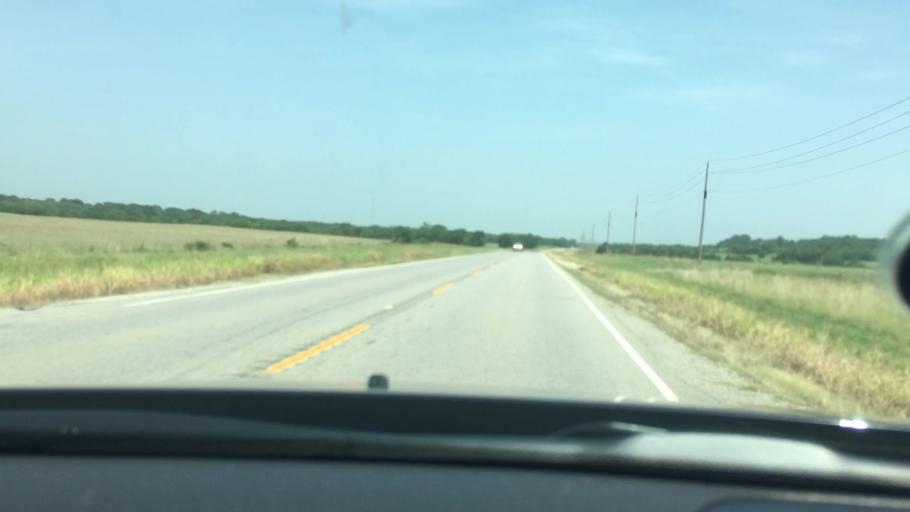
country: US
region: Oklahoma
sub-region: Atoka County
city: Atoka
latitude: 34.4330
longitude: -96.1989
